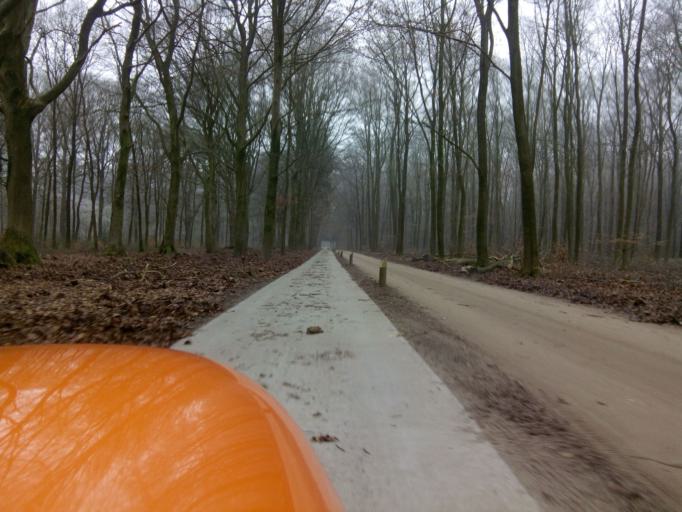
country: NL
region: Gelderland
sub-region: Gemeente Putten
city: Putten
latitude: 52.2386
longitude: 5.6477
